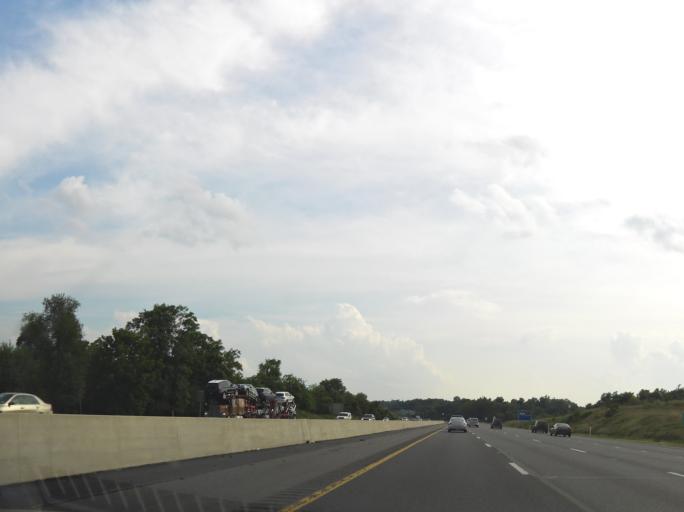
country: US
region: West Virginia
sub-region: Berkeley County
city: Martinsburg
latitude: 39.4743
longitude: -77.9861
